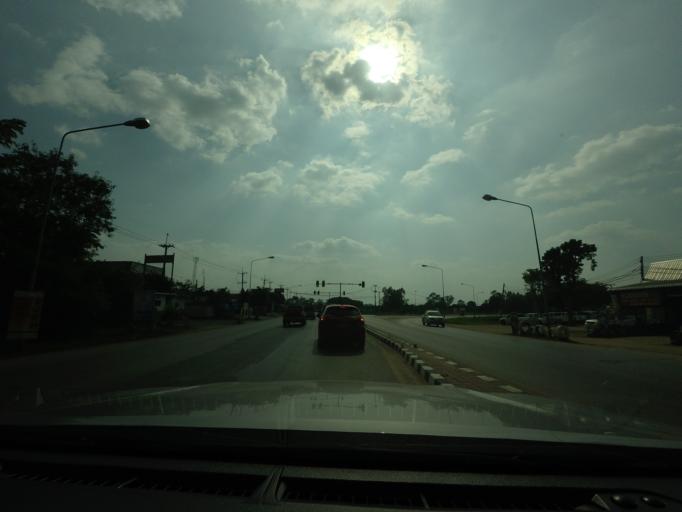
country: TH
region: Phitsanulok
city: Bang Rakam
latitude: 16.7469
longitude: 100.1117
